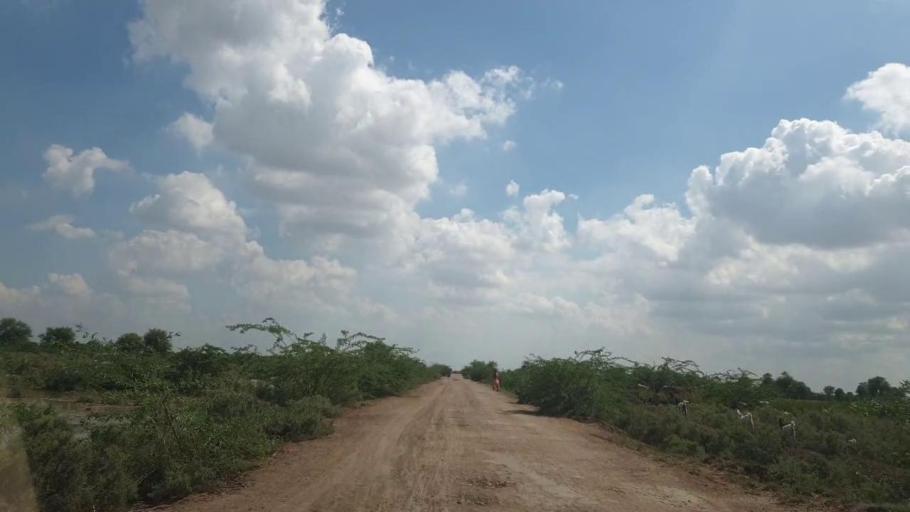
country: PK
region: Sindh
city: Pithoro
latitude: 25.6073
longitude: 69.4085
